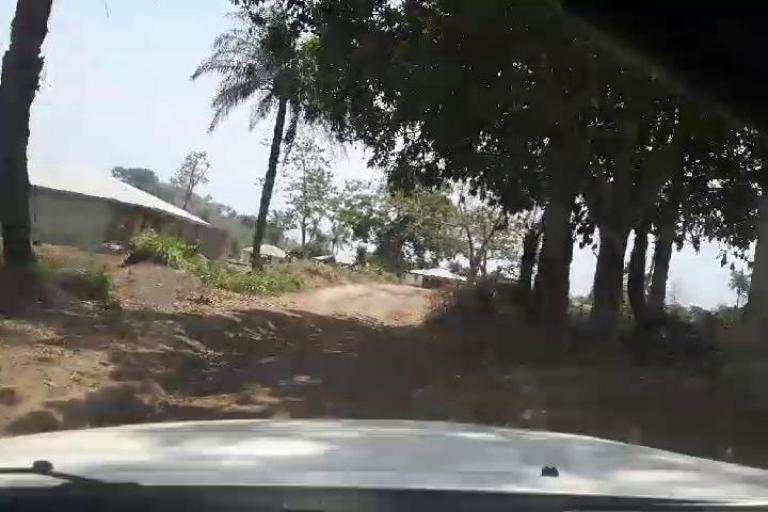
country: SL
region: Northern Province
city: Alikalia
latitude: 9.0649
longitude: -11.4847
